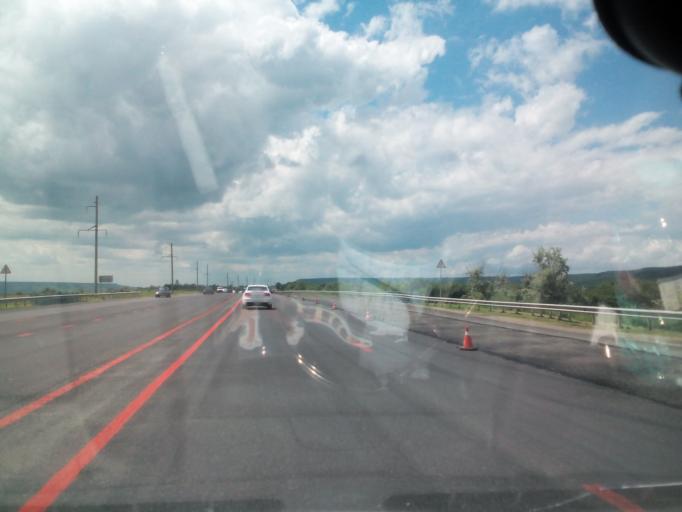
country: RU
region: Stavropol'skiy
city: Tatarka
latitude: 44.9539
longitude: 41.9585
